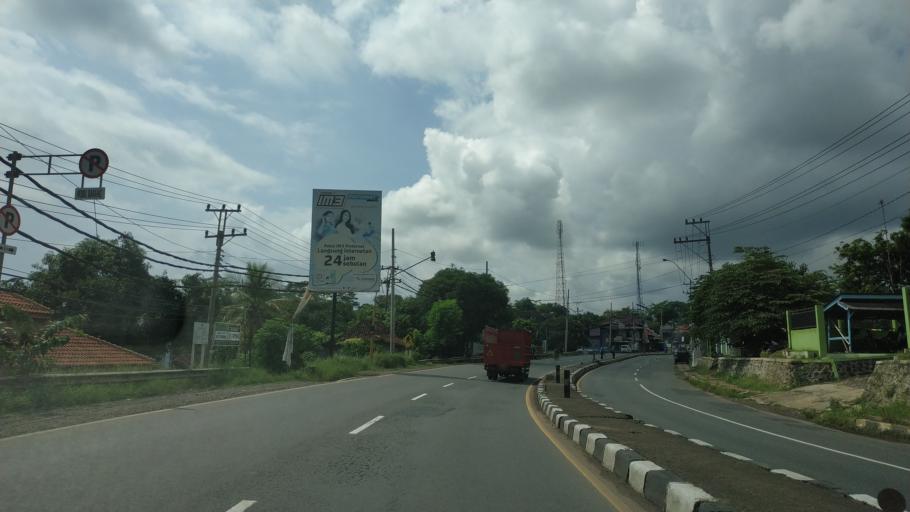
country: ID
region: Central Java
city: Pekalongan
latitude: -6.9335
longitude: 109.7720
